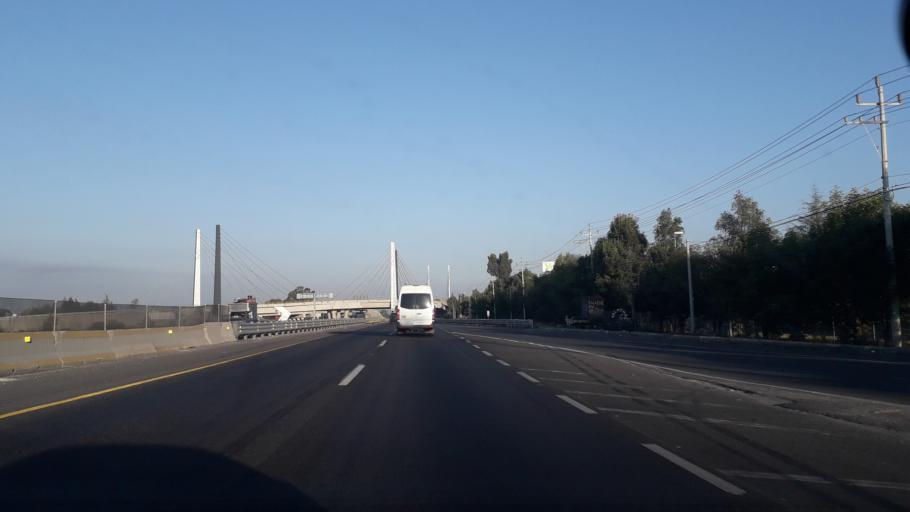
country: MX
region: Puebla
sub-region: Puebla
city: Primero de Mayo
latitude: 19.0647
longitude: -98.1042
